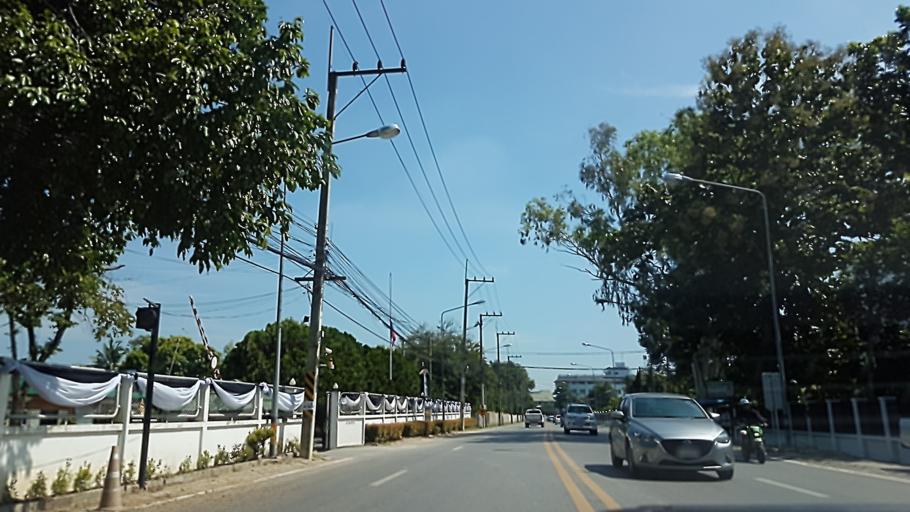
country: TH
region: Chiang Mai
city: Chiang Mai
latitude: 18.8181
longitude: 98.9784
